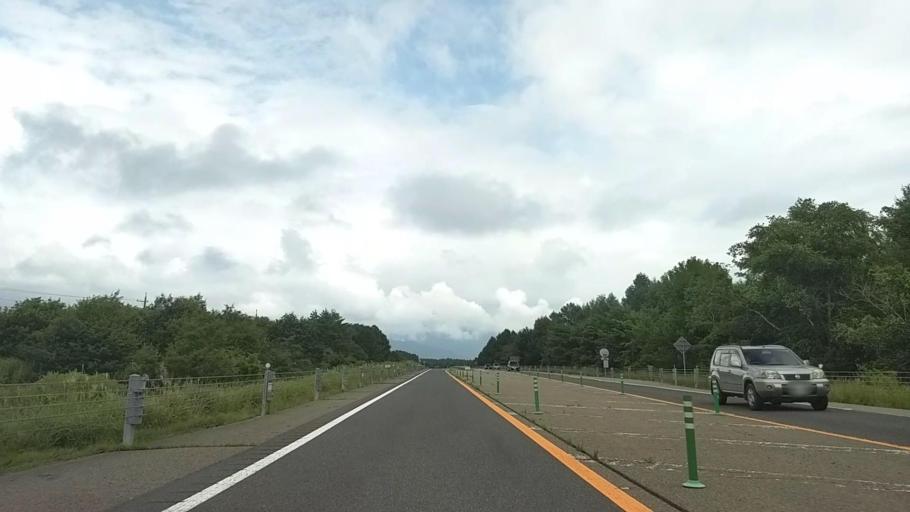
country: JP
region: Yamanashi
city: Fujikawaguchiko
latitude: 35.4492
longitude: 138.8030
